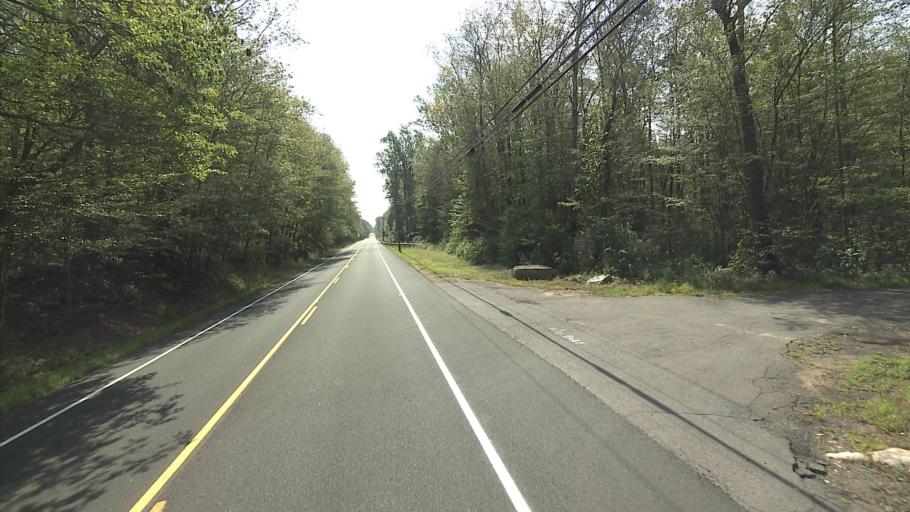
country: US
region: Connecticut
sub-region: Middlesex County
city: Durham
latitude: 41.3965
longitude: -72.6522
